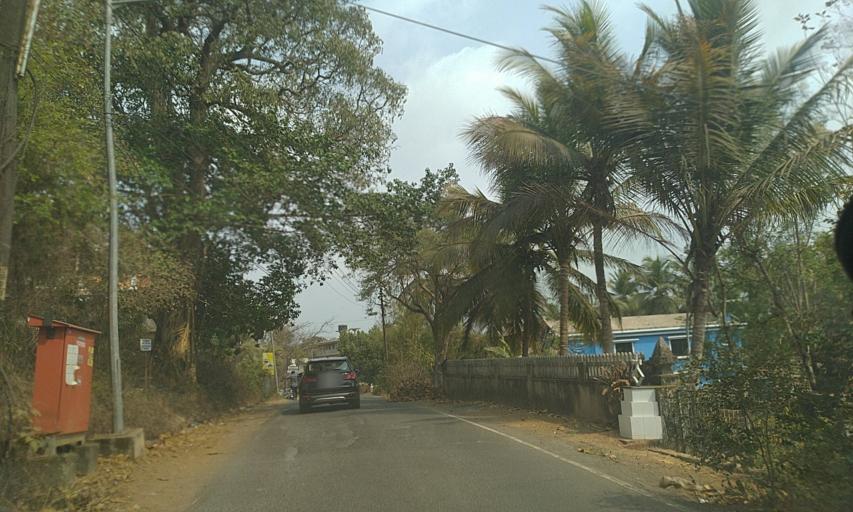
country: IN
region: Goa
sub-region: South Goa
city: Raia
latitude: 15.3073
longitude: 73.9479
